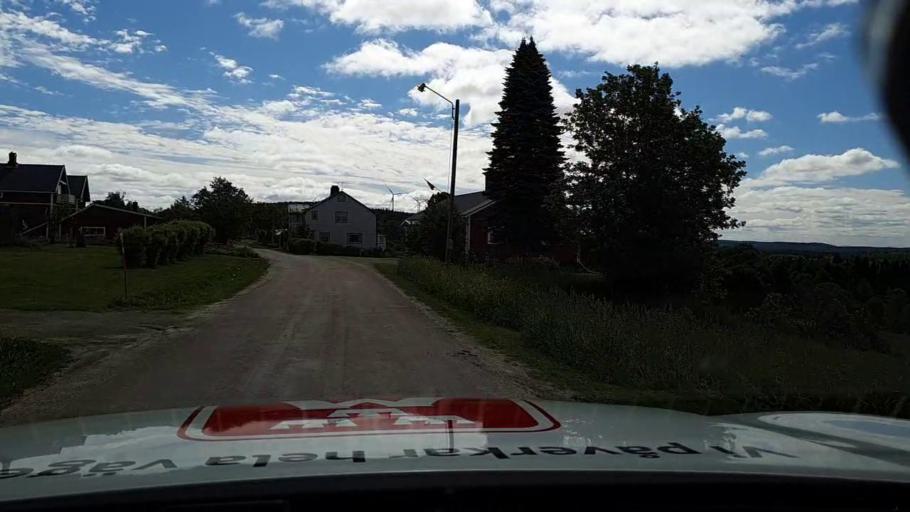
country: SE
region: Jaemtland
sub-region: Braecke Kommun
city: Braecke
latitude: 62.7664
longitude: 15.4944
